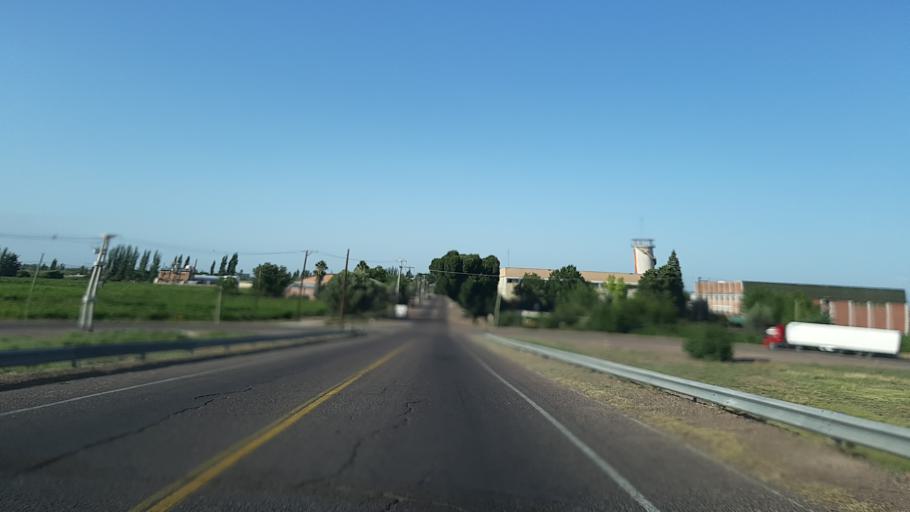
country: AR
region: Mendoza
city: San Martin
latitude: -33.0413
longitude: -68.5209
